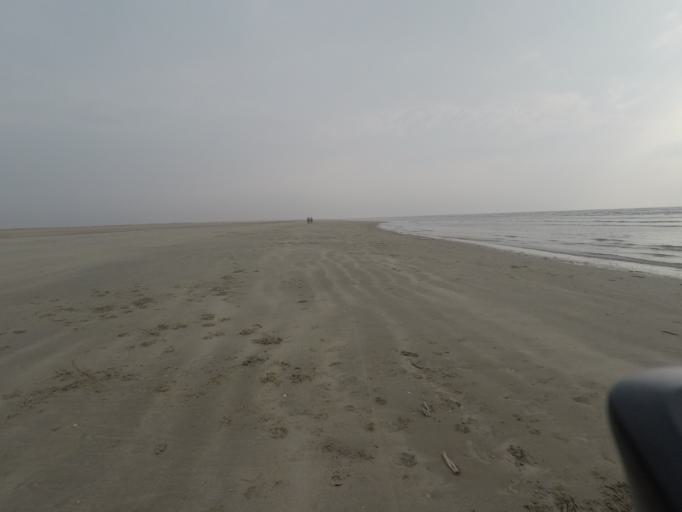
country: DE
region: Schleswig-Holstein
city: List
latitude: 55.1619
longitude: 8.4765
